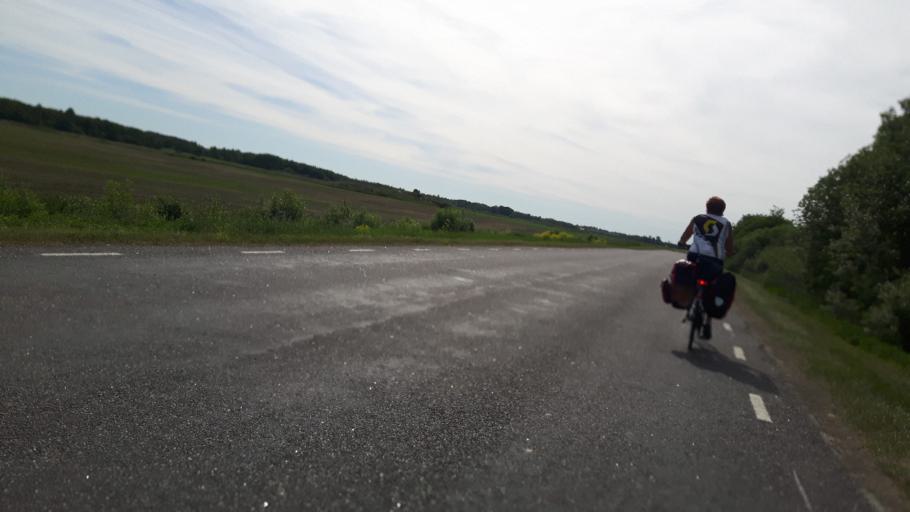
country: EE
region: Harju
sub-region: Maardu linn
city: Maardu
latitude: 59.4260
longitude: 25.0622
